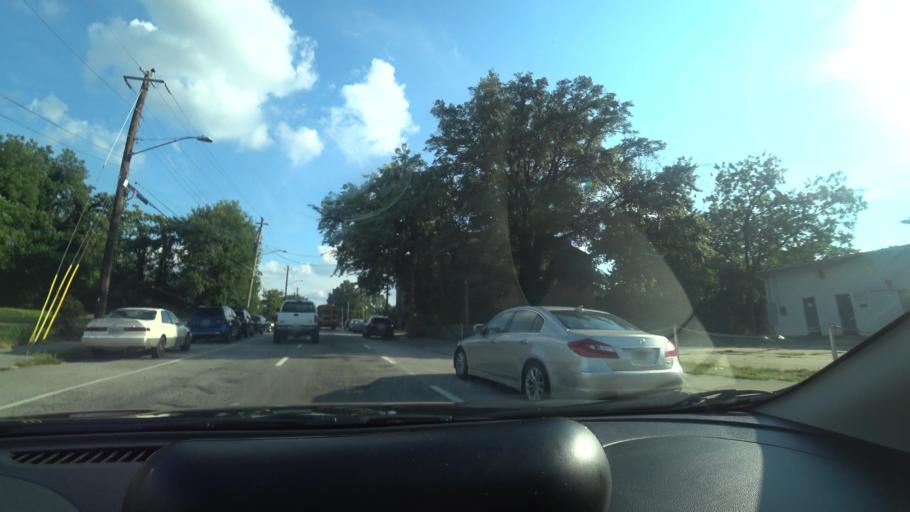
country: US
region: Georgia
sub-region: Fulton County
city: Atlanta
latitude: 33.7366
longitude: -84.3946
